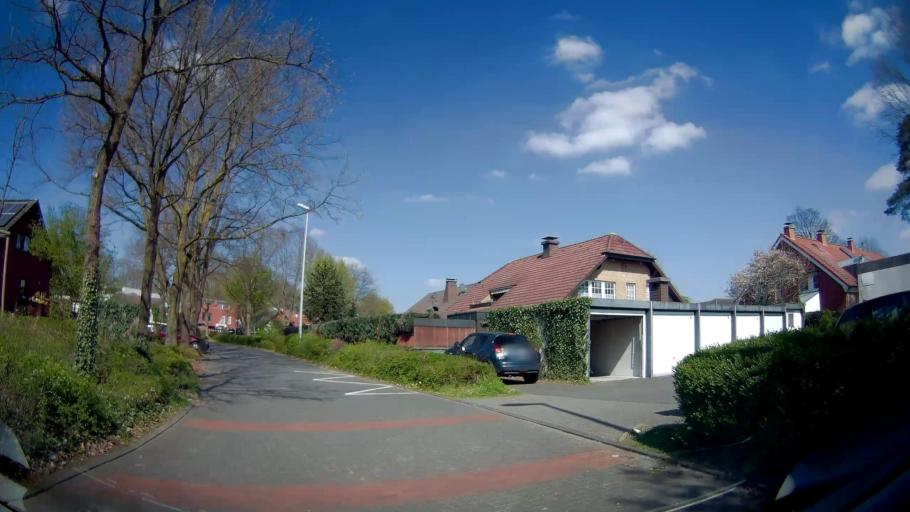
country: DE
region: North Rhine-Westphalia
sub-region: Regierungsbezirk Munster
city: Klein Reken
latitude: 51.7342
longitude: 7.0444
